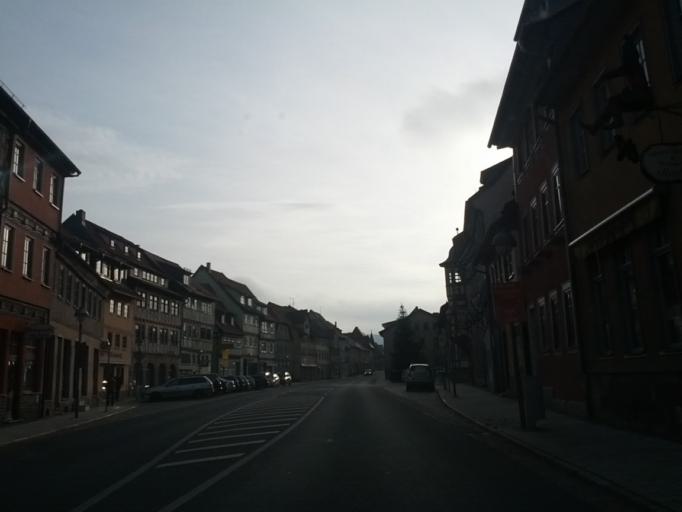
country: DE
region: Thuringia
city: Wasungen
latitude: 50.6641
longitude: 10.3681
